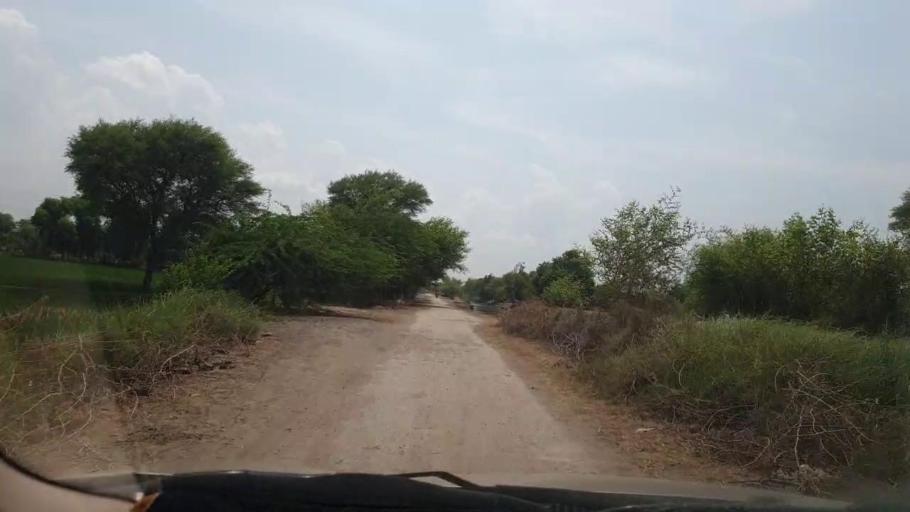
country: PK
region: Sindh
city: Larkana
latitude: 27.5834
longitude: 68.1161
